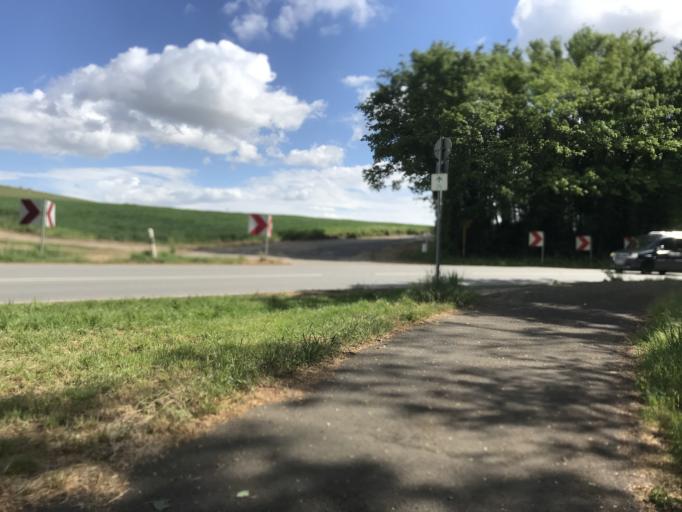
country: DE
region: Rheinland-Pfalz
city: Nieder-Olm
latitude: 49.9175
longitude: 8.2047
